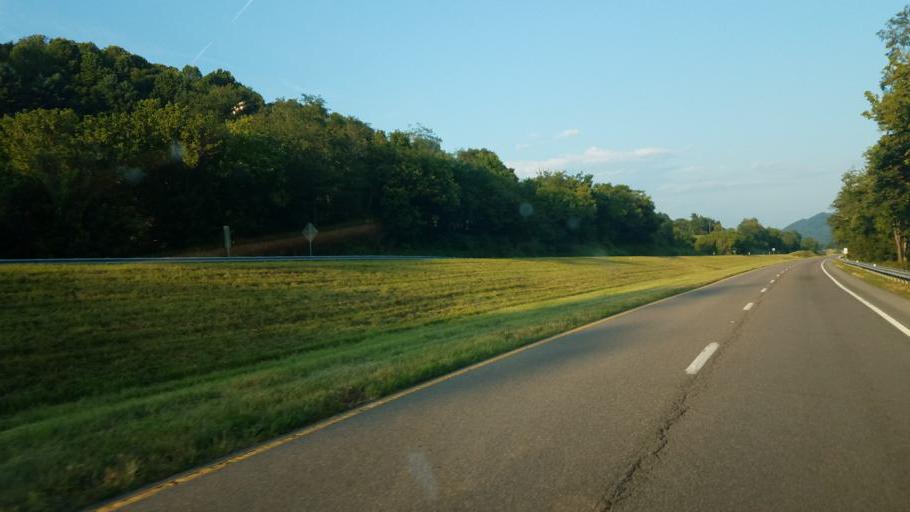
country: US
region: Virginia
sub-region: Scott County
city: Gate City
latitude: 36.6349
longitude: -82.6365
